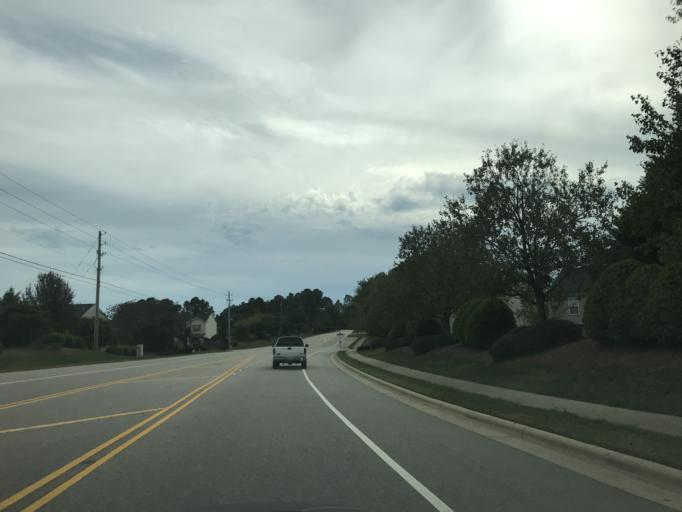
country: US
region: North Carolina
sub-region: Wake County
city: Rolesville
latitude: 35.8788
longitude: -78.5097
